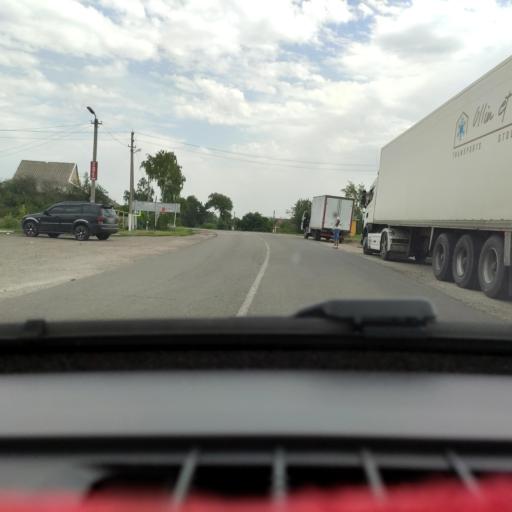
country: RU
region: Voronezj
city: Davydovka
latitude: 51.2151
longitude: 39.5228
